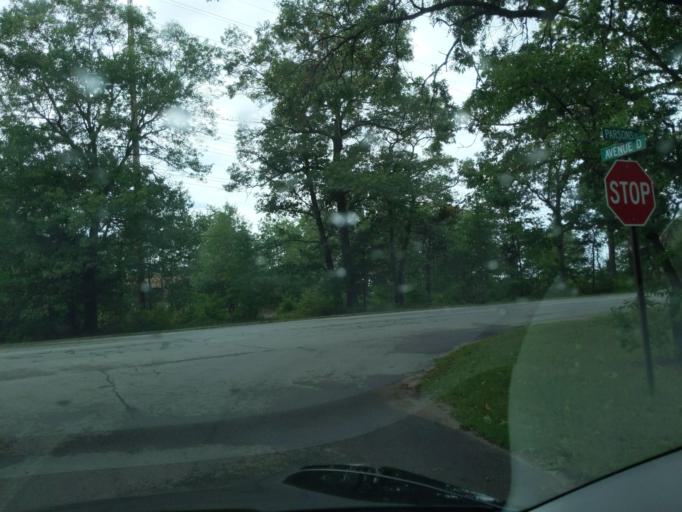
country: US
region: Michigan
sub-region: Grand Traverse County
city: Traverse City
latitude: 44.7497
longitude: -85.5736
